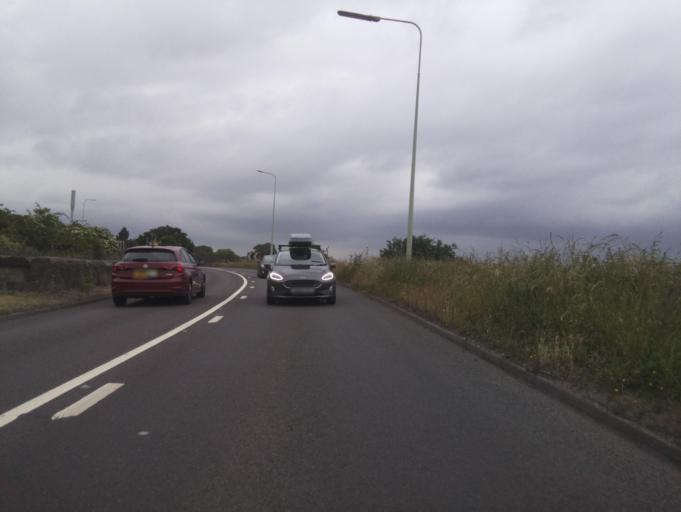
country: GB
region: England
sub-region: Staffordshire
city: Stafford
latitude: 52.7742
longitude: -2.1098
